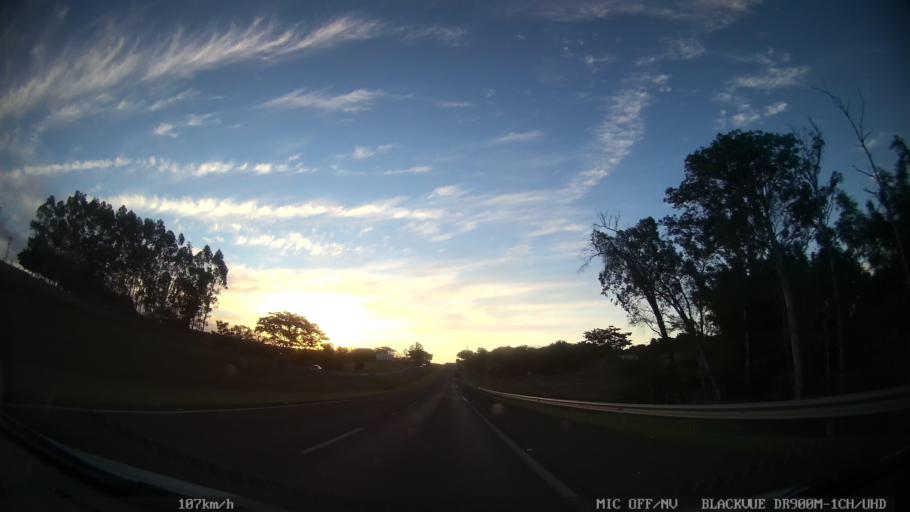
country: BR
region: Sao Paulo
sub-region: Pindorama
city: Pindorama
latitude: -21.2183
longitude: -48.9218
